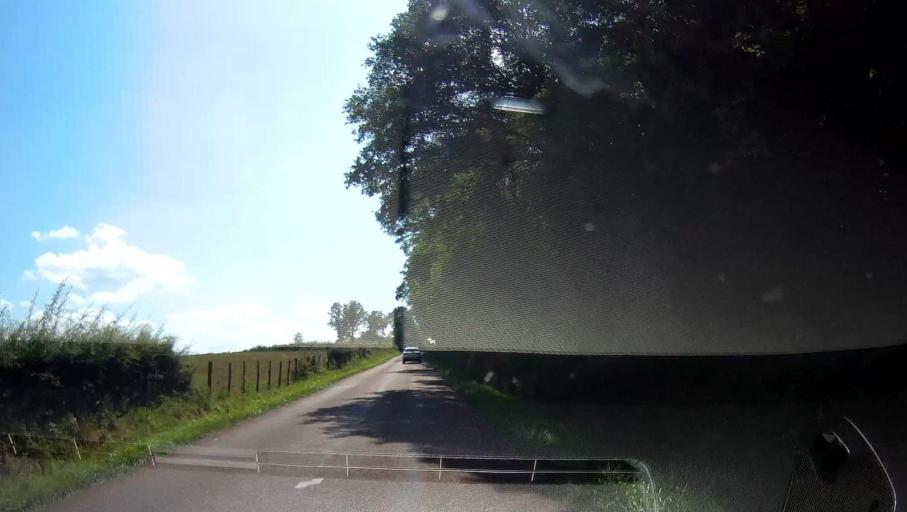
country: FR
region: Bourgogne
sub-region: Departement de Saone-et-Loire
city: Saint-Leger-sur-Dheune
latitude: 46.8748
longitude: 4.6346
